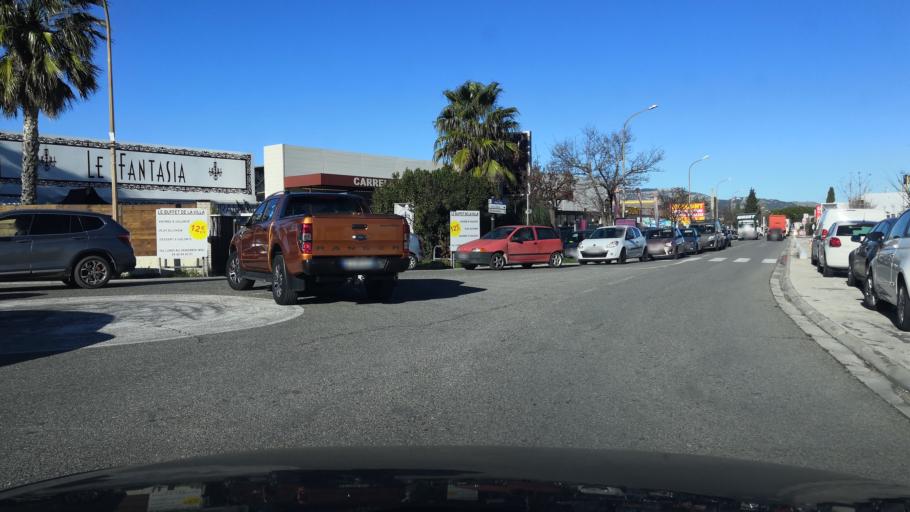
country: FR
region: Provence-Alpes-Cote d'Azur
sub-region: Departement des Bouches-du-Rhone
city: Gemenos
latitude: 43.2842
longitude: 5.6021
